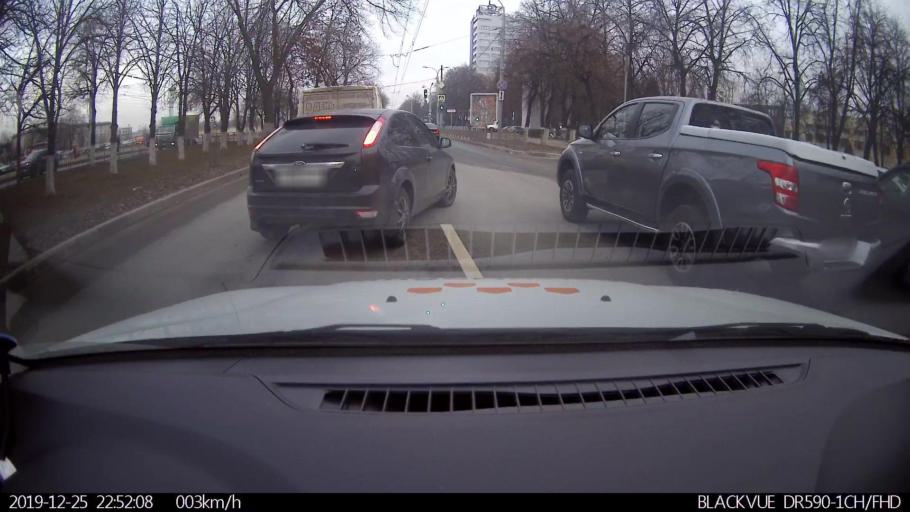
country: RU
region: Nizjnij Novgorod
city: Gorbatovka
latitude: 56.2482
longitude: 43.8799
